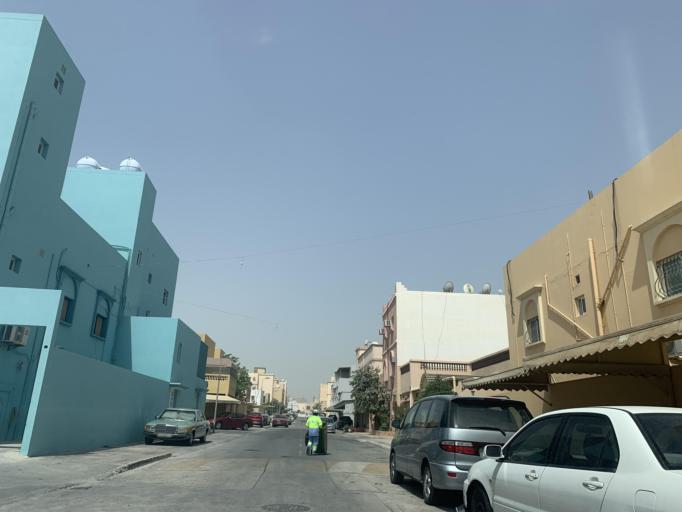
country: BH
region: Northern
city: Madinat `Isa
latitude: 26.1504
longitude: 50.5221
